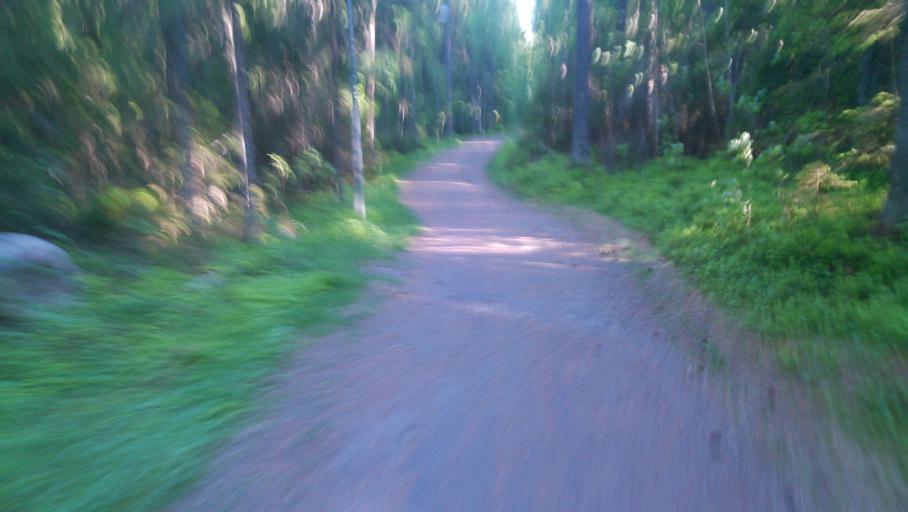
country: SE
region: Vaesterbotten
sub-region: Umea Kommun
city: Ersmark
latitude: 63.8384
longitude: 20.3080
